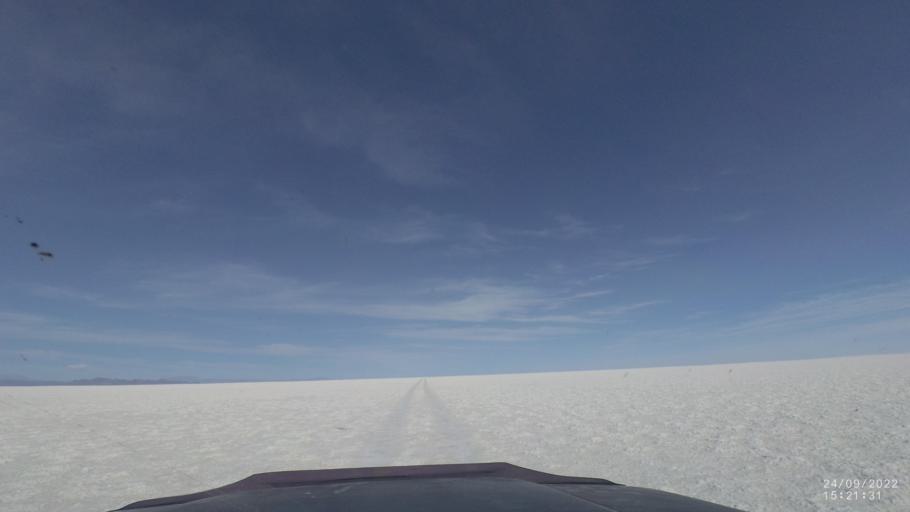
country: BO
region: Potosi
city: Colchani
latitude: -20.0209
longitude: -67.3885
